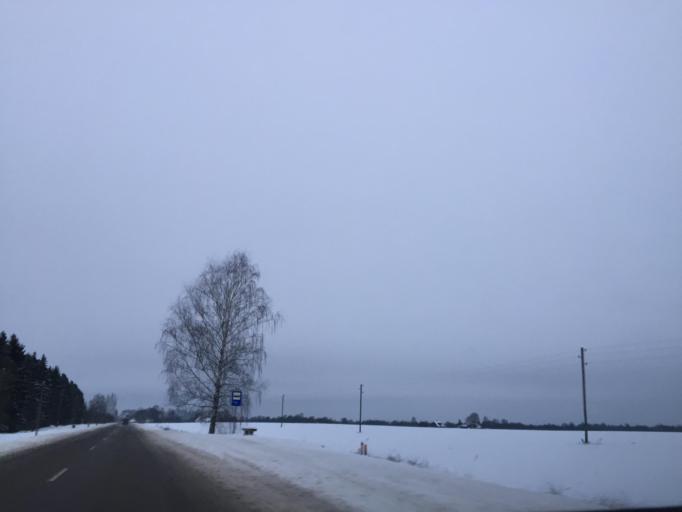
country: LV
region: Smiltene
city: Smiltene
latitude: 57.4343
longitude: 25.8019
